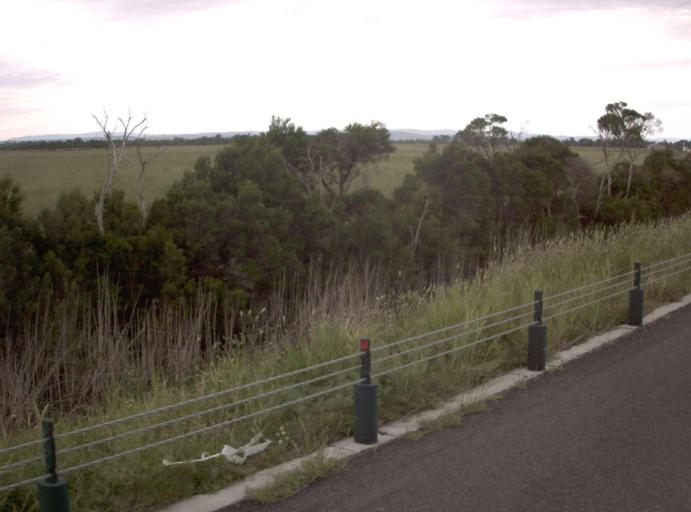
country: AU
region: Victoria
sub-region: Cardinia
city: Koo-Wee-Rup
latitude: -38.2123
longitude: 145.4649
